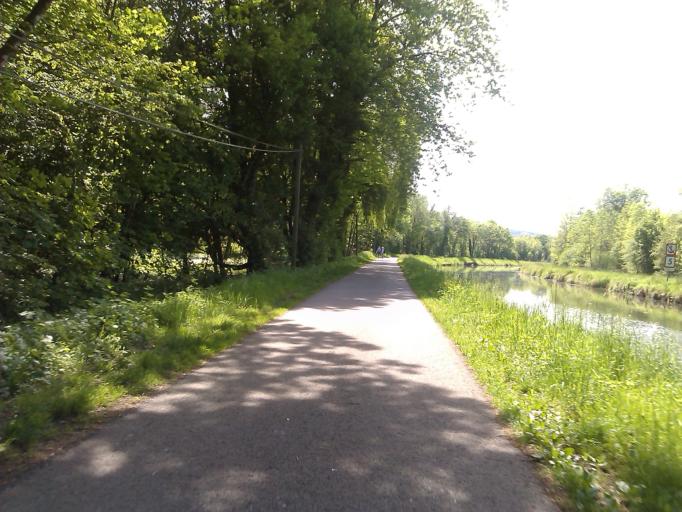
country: FR
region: Franche-Comte
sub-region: Departement du Doubs
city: Avanne-Aveney
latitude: 47.1835
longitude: 5.9576
